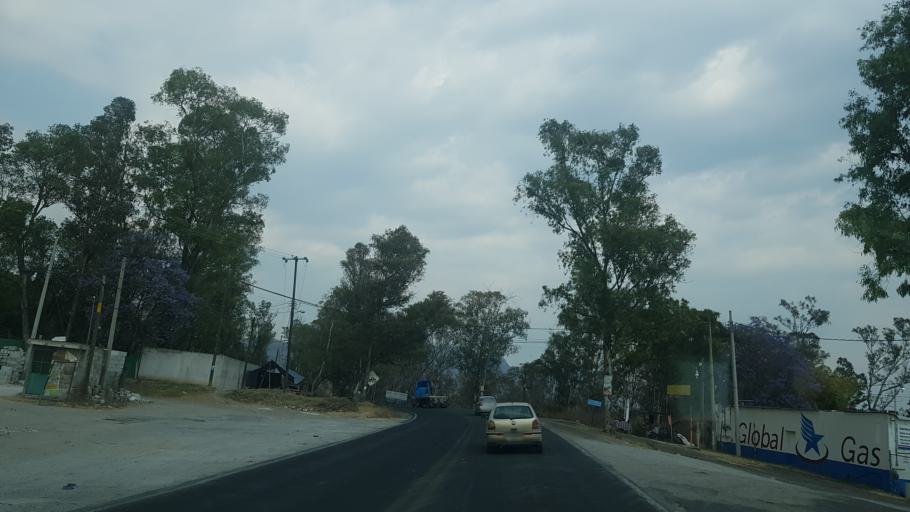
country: MX
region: Puebla
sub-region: Santa Isabel Cholula
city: Santa Ana Acozautla
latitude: 18.9444
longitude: -98.3921
